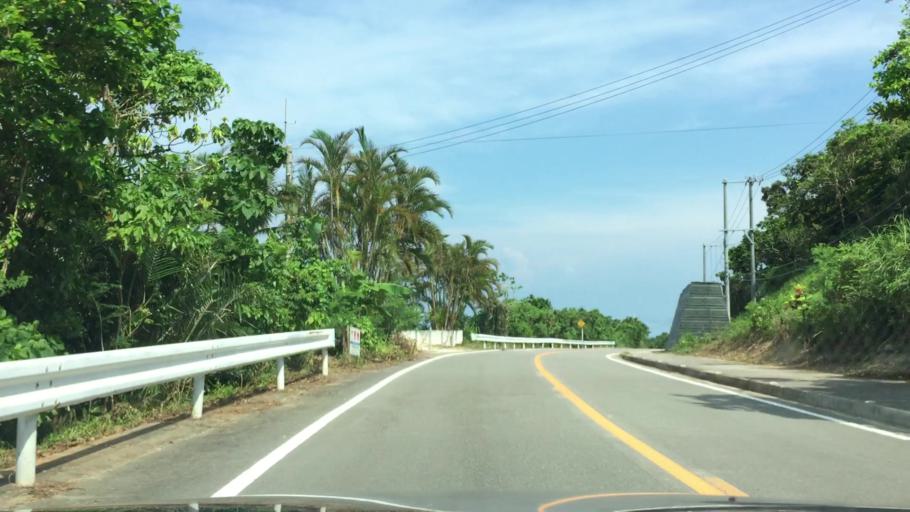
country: JP
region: Okinawa
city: Ishigaki
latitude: 24.5160
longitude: 124.2617
